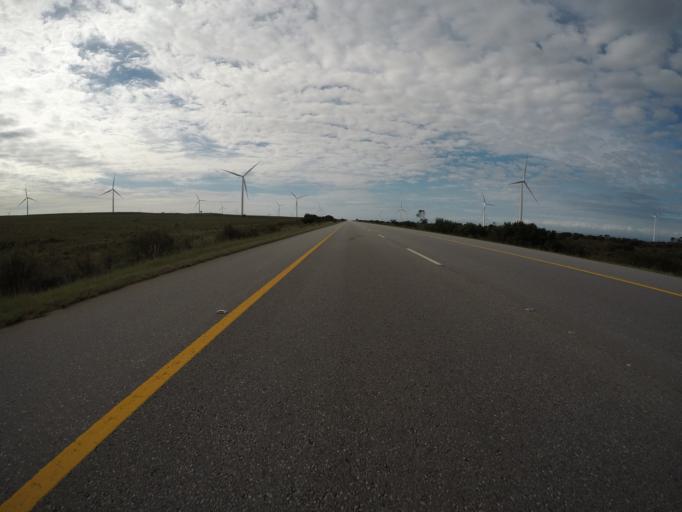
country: ZA
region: Eastern Cape
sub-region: Cacadu District Municipality
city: Kruisfontein
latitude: -34.0163
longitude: 24.8131
